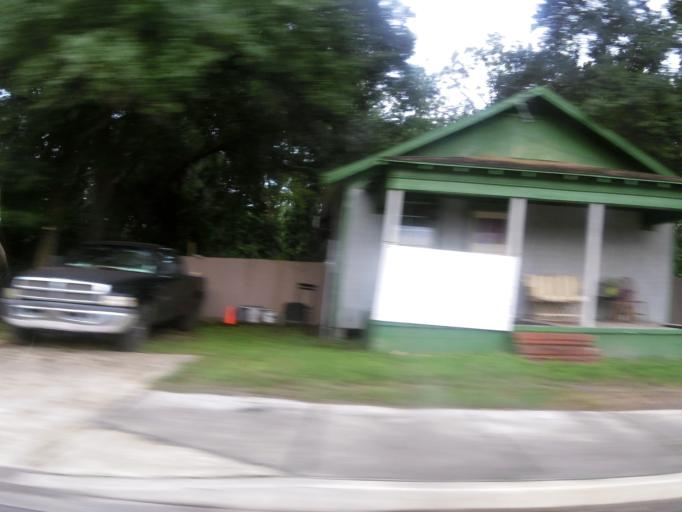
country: US
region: Florida
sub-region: Duval County
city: Jacksonville
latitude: 30.3417
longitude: -81.7055
